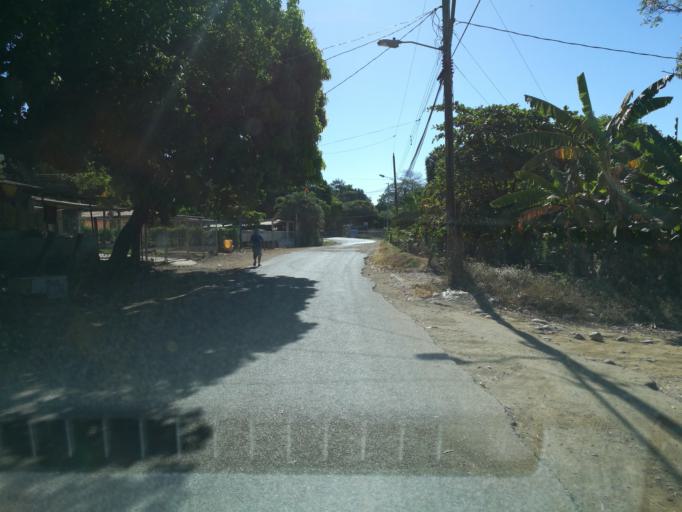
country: CR
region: Guanacaste
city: Juntas
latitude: 10.0991
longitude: -84.9902
